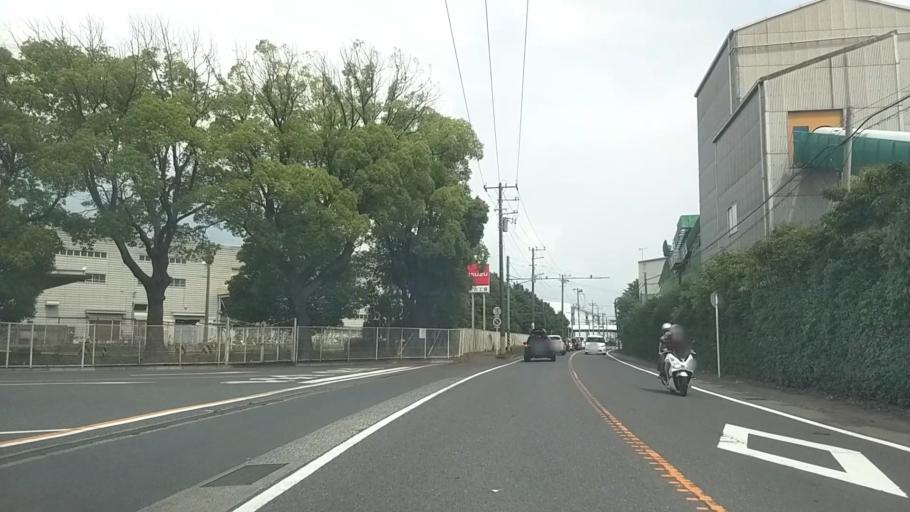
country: JP
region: Kanagawa
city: Fujisawa
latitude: 35.3956
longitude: 139.4522
